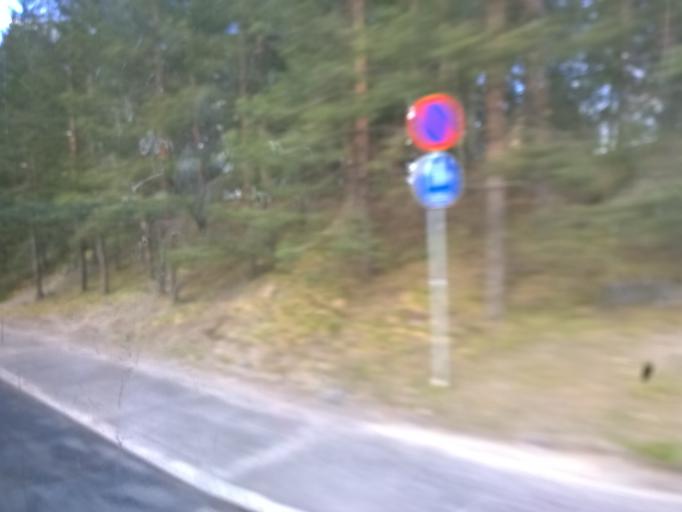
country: FI
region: Pirkanmaa
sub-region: Tampere
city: Tampere
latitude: 61.4698
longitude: 23.7748
